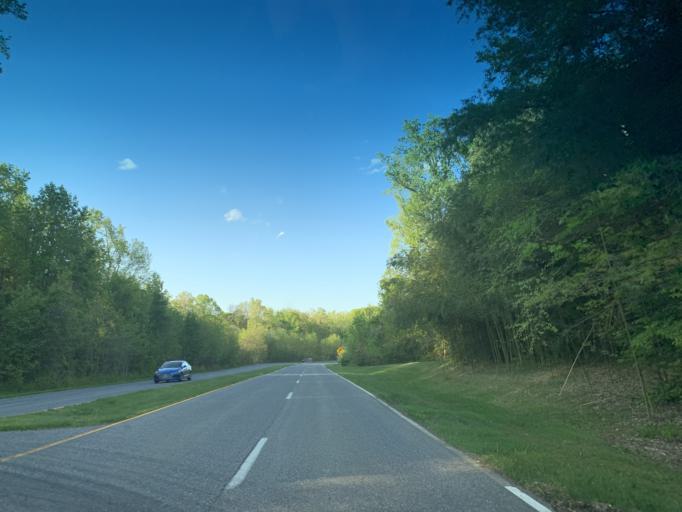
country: US
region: Maryland
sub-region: Harford County
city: Aberdeen
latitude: 39.5321
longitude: -76.1949
